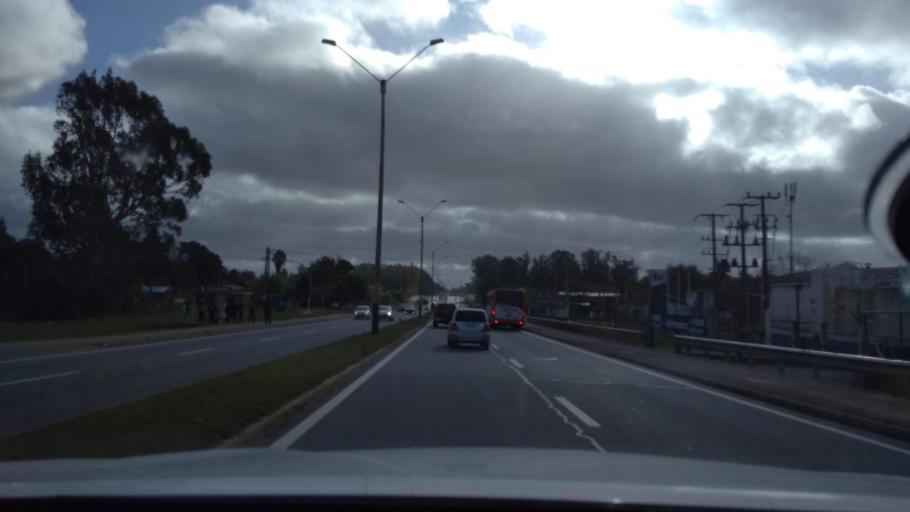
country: UY
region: Canelones
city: Colonia Nicolich
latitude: -34.8098
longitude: -56.0403
